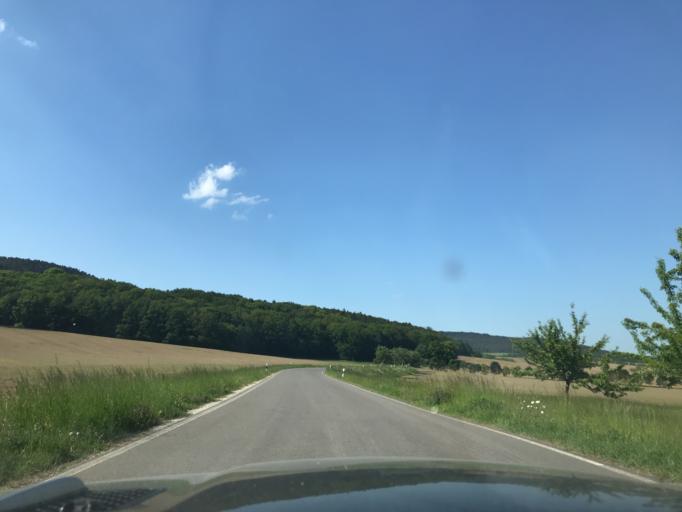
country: DE
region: Thuringia
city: Plaue
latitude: 50.7575
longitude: 10.9461
